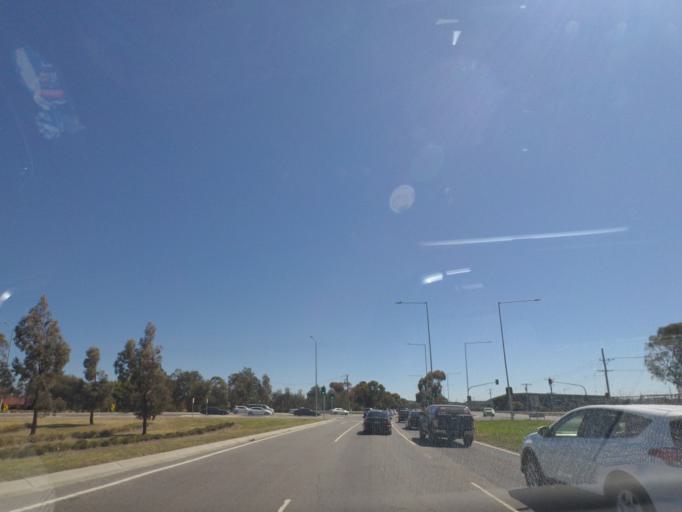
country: AU
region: Victoria
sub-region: Hume
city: Craigieburn
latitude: -37.5978
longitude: 144.9431
